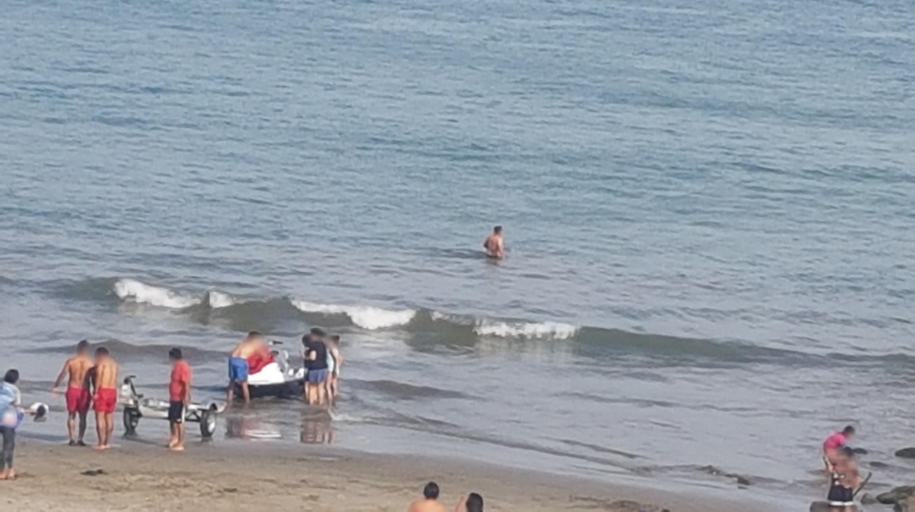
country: PE
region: Ancash
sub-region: Provincia de Santa
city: Samanco
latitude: -9.3228
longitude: -78.4736
